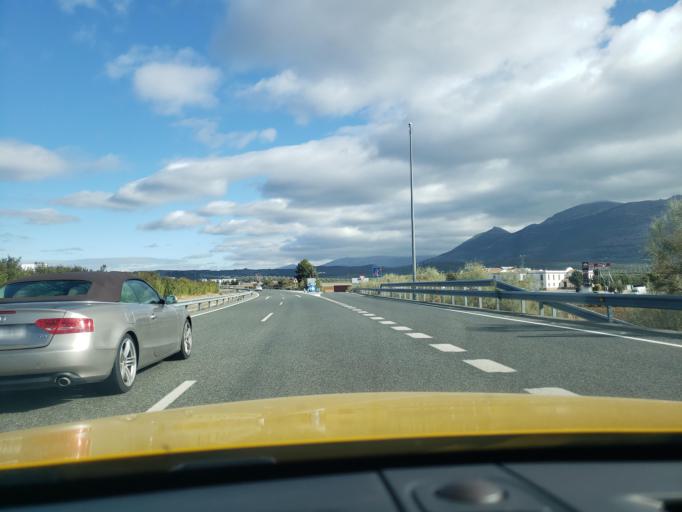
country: ES
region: Andalusia
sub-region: Provincia de Malaga
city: Villanueva del Trabuco
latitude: 37.0672
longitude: -4.3296
